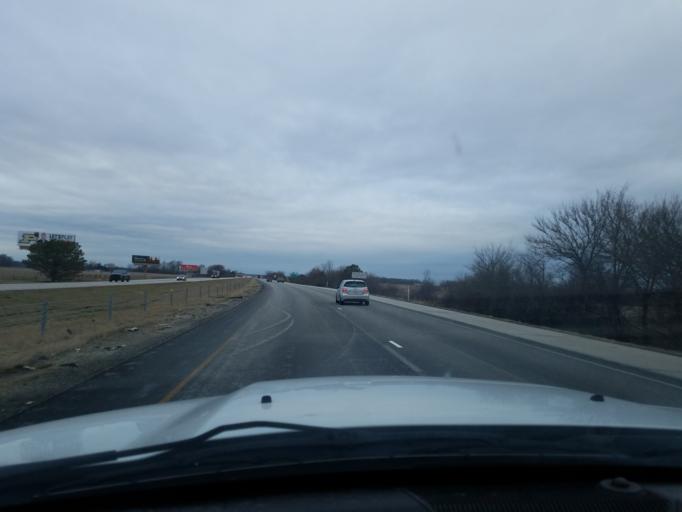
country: US
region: Indiana
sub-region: Clinton County
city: Mulberry
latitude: 40.2698
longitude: -86.6641
